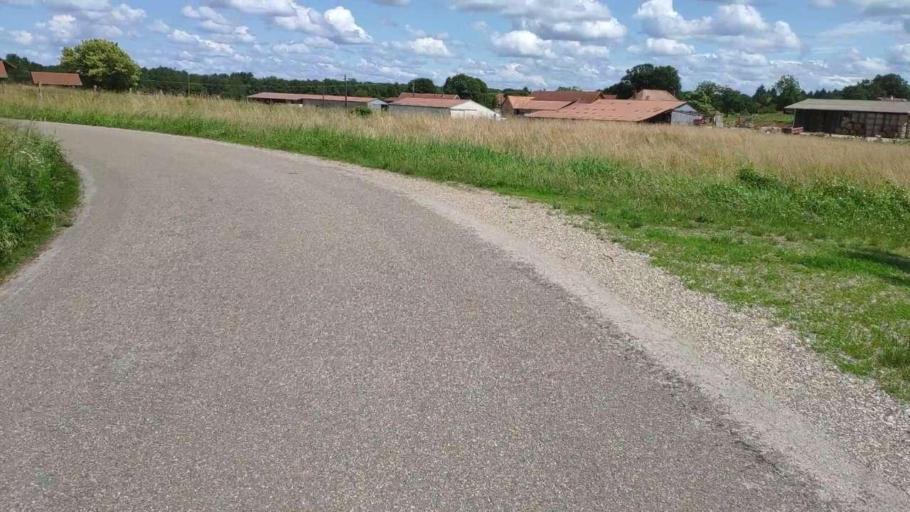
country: FR
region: Franche-Comte
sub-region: Departement du Jura
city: Chaussin
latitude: 46.8774
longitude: 5.4809
